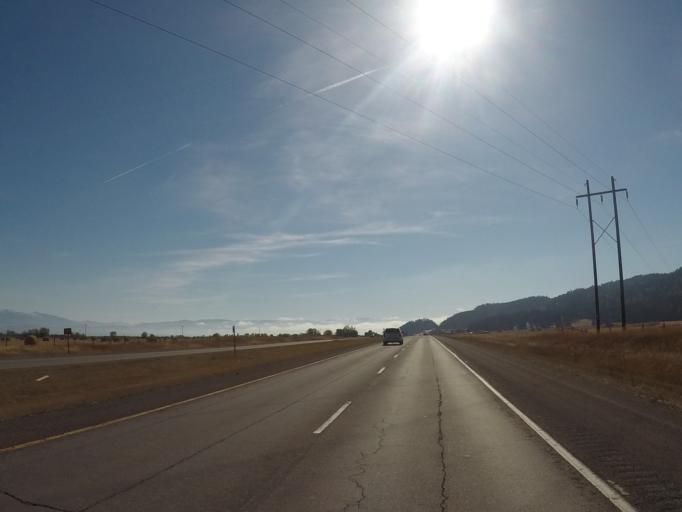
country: US
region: Montana
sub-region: Flathead County
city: Somers
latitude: 48.1115
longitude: -114.2508
